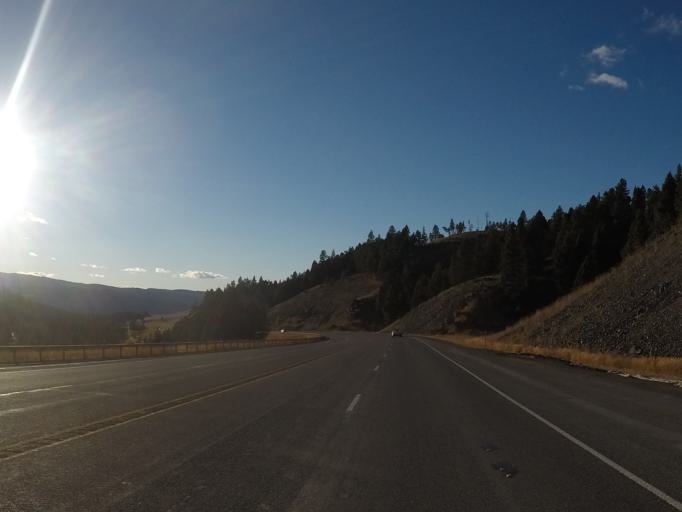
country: US
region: Montana
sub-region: Lewis and Clark County
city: Helena West Side
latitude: 46.5590
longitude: -112.3438
